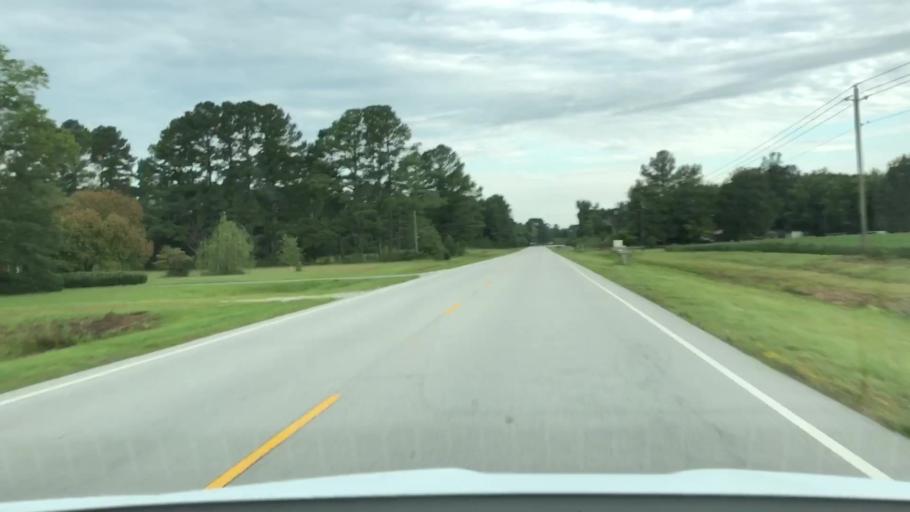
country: US
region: North Carolina
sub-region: Jones County
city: Trenton
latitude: 35.0155
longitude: -77.2963
